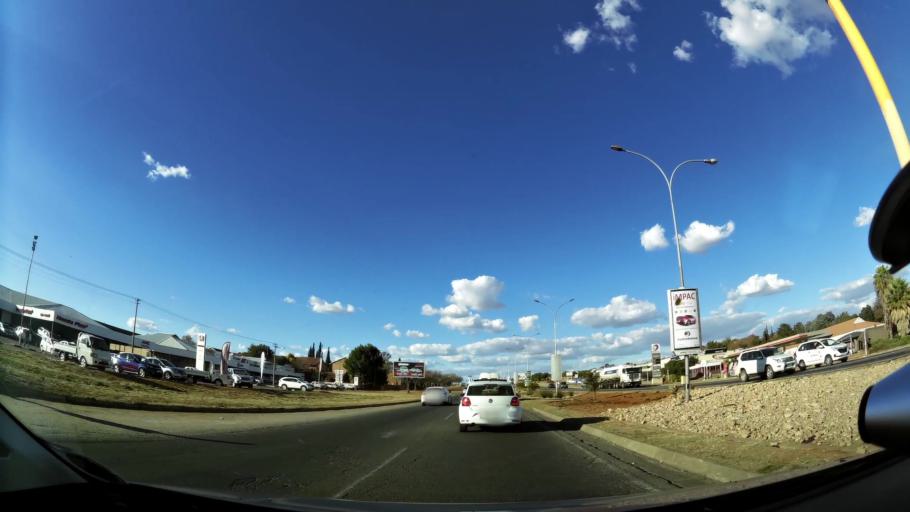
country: ZA
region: North-West
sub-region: Dr Kenneth Kaunda District Municipality
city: Klerksdorp
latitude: -26.8543
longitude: 26.6815
